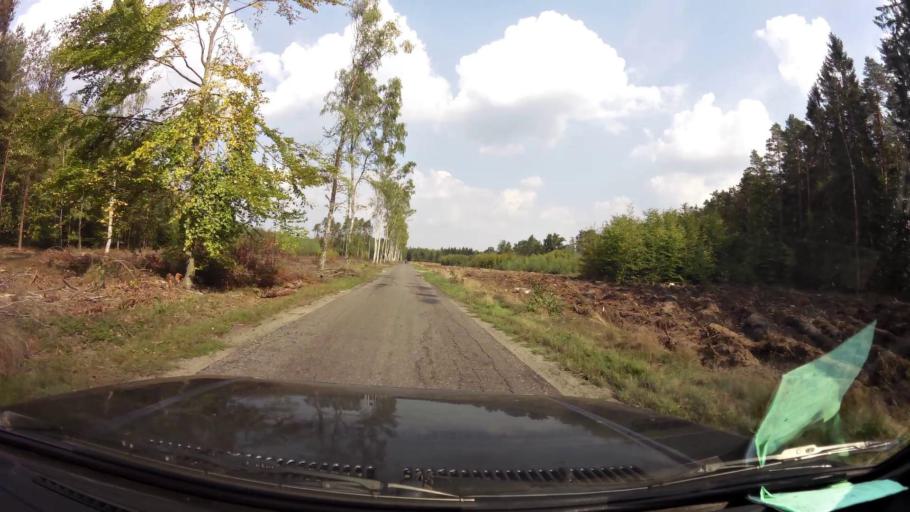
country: PL
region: West Pomeranian Voivodeship
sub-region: Powiat koszalinski
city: Bobolice
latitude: 54.0867
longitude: 16.4815
